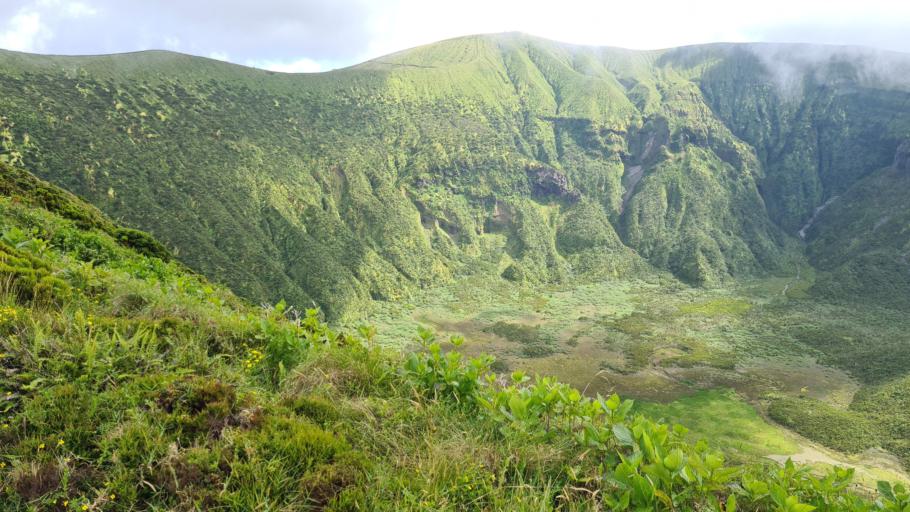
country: PT
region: Azores
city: Ribeira Grande
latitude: 38.5931
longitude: -28.7090
